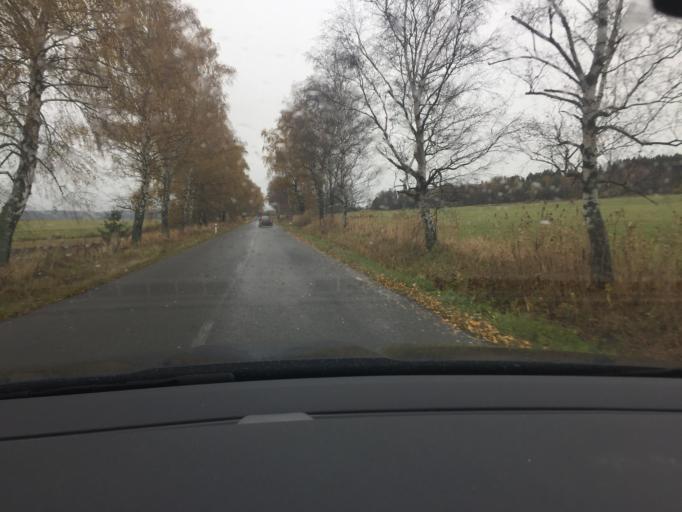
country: SK
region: Presovsky
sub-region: Okres Presov
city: Kezmarok
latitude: 49.1800
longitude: 20.4000
